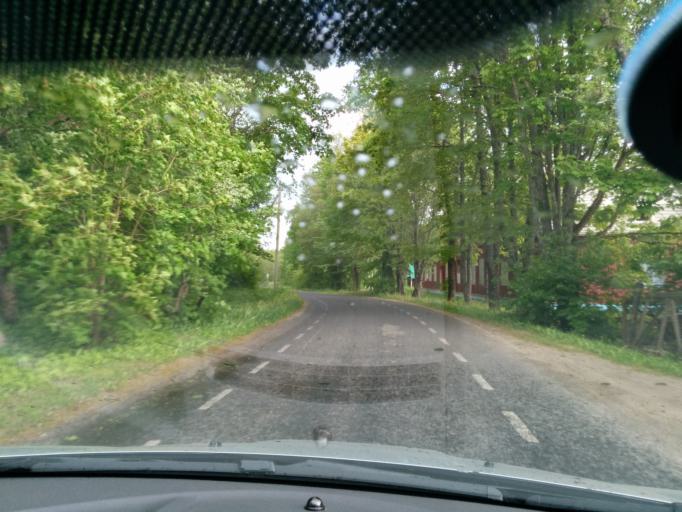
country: EE
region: Harju
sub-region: Loksa linn
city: Loksa
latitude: 59.6418
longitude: 25.7573
